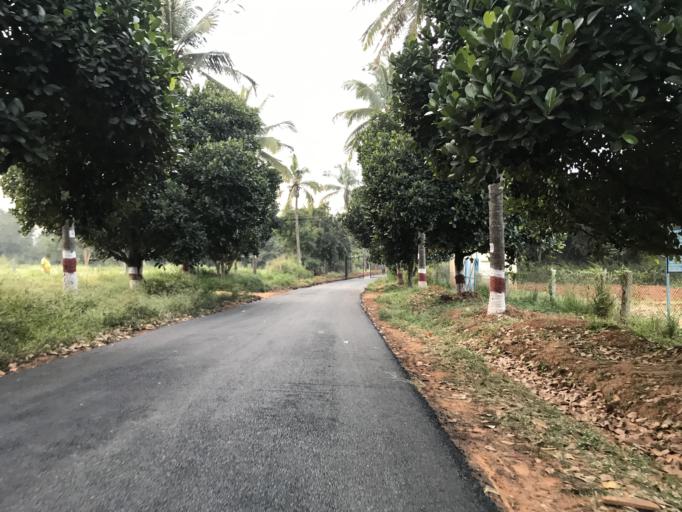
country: IN
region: Karnataka
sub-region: Bangalore Urban
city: Yelahanka
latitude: 13.0808
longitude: 77.5692
